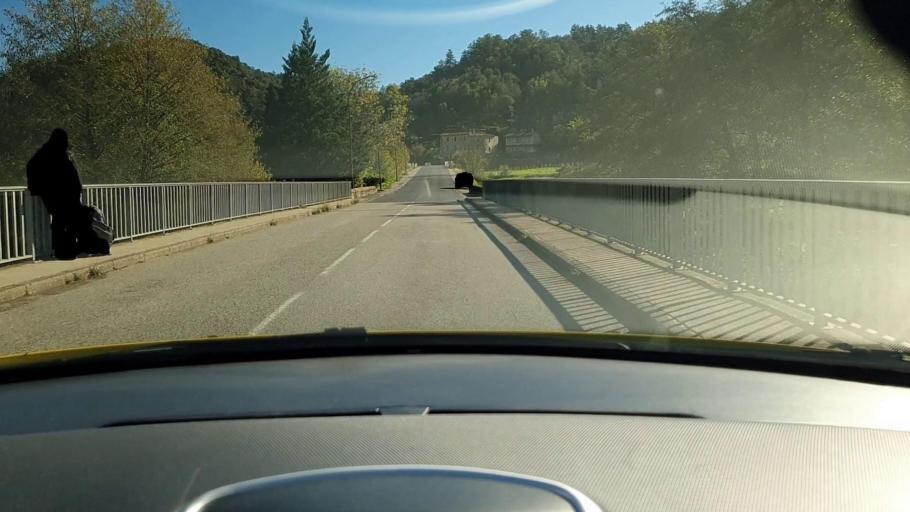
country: FR
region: Languedoc-Roussillon
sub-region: Departement du Gard
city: Le Vigan
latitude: 43.9903
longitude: 3.6094
